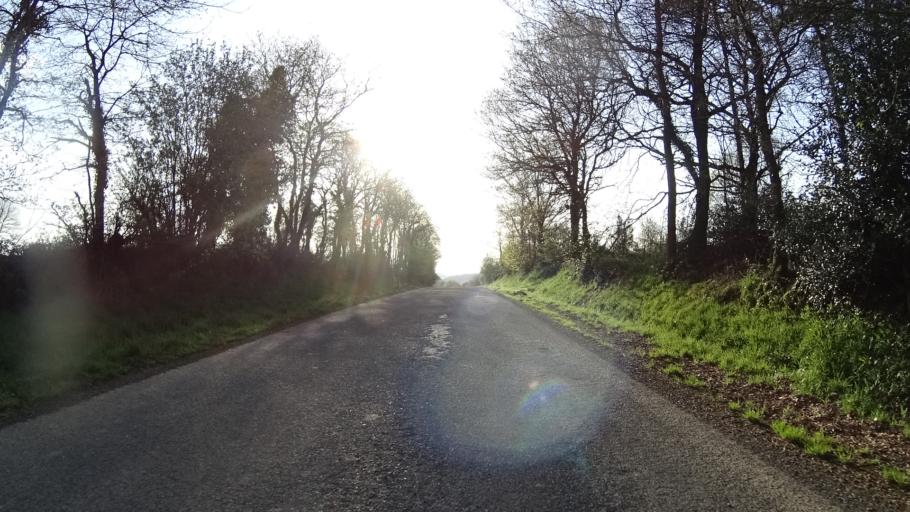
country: FR
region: Brittany
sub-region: Departement du Finistere
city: Sizun
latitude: 48.4286
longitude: -4.0710
